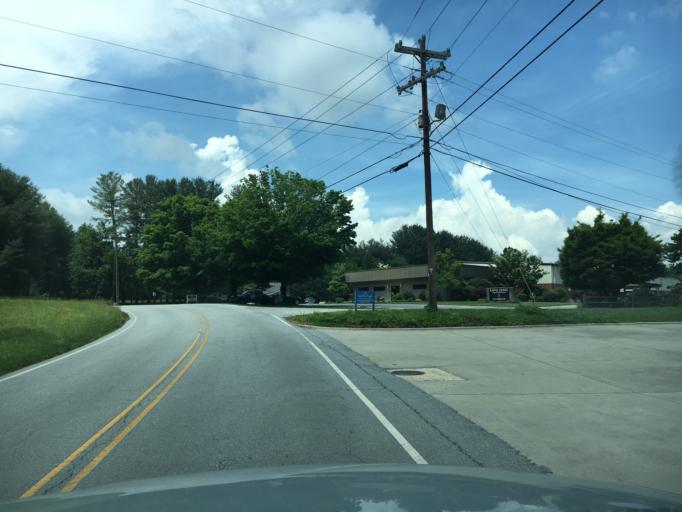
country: US
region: North Carolina
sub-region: Henderson County
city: Mills River
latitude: 35.3772
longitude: -82.5740
